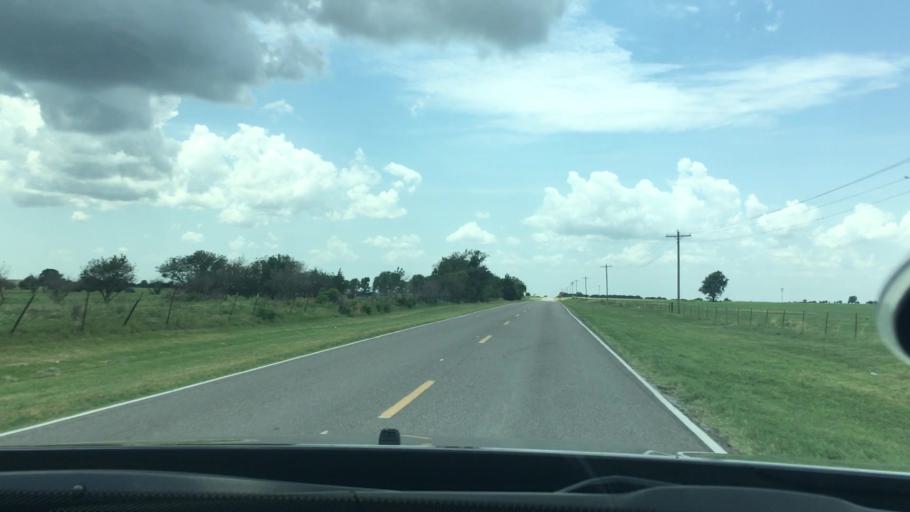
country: US
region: Oklahoma
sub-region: Carter County
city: Wilson
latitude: 33.9403
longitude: -97.3815
